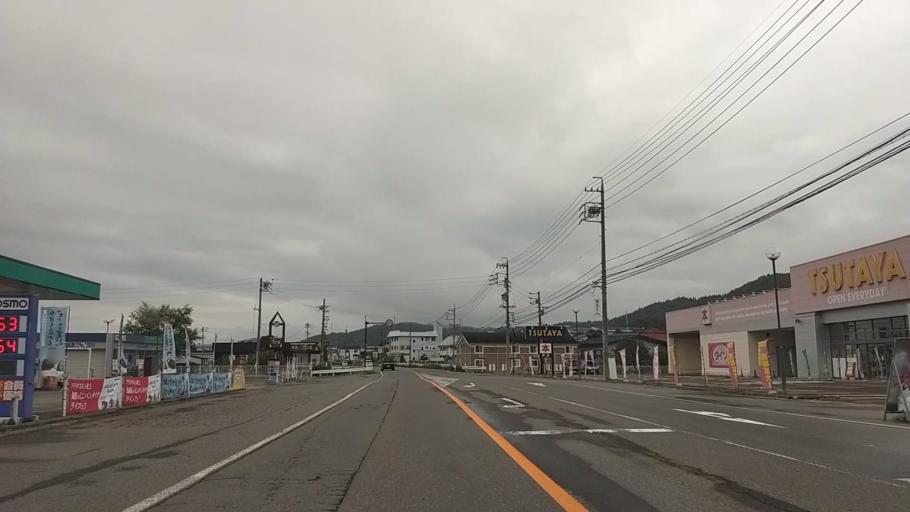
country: JP
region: Nagano
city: Iiyama
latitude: 36.8313
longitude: 138.3554
